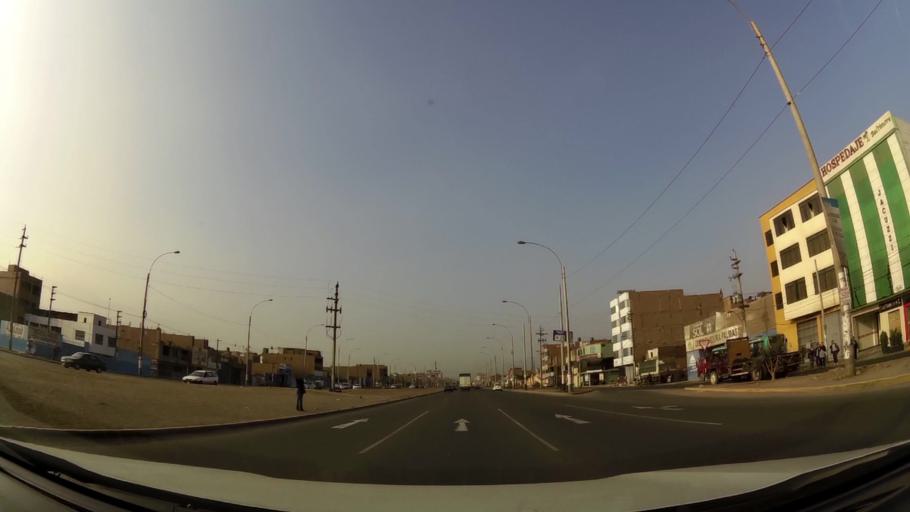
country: PE
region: Lima
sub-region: Lima
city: Independencia
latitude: -11.9873
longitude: -77.1031
